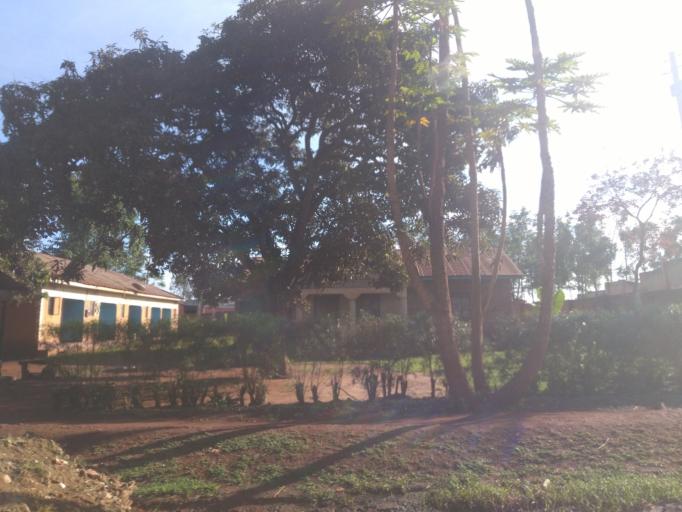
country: UG
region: Eastern Region
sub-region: Jinja District
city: Jinja
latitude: 0.4562
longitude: 33.1858
